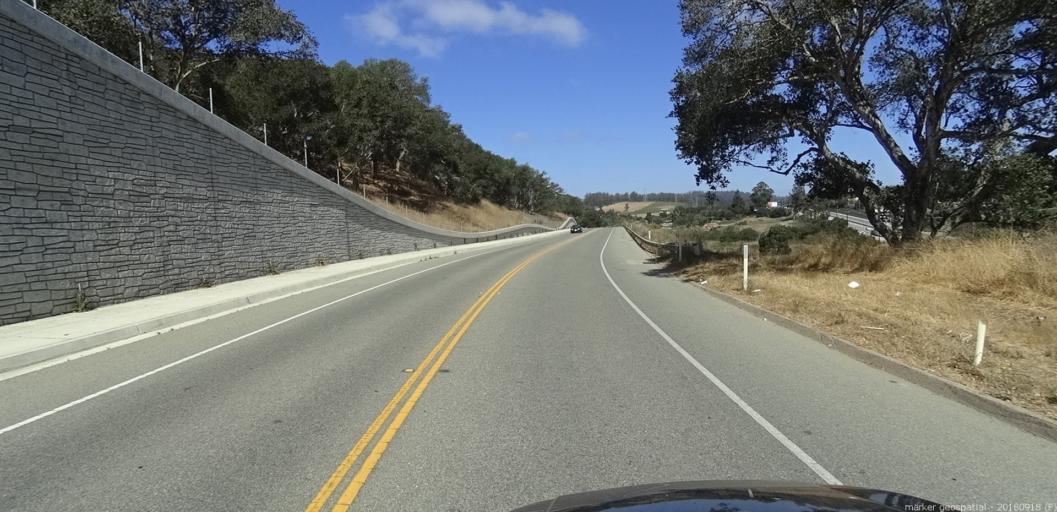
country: US
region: California
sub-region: Monterey County
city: Prunedale
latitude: 36.7704
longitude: -121.6698
